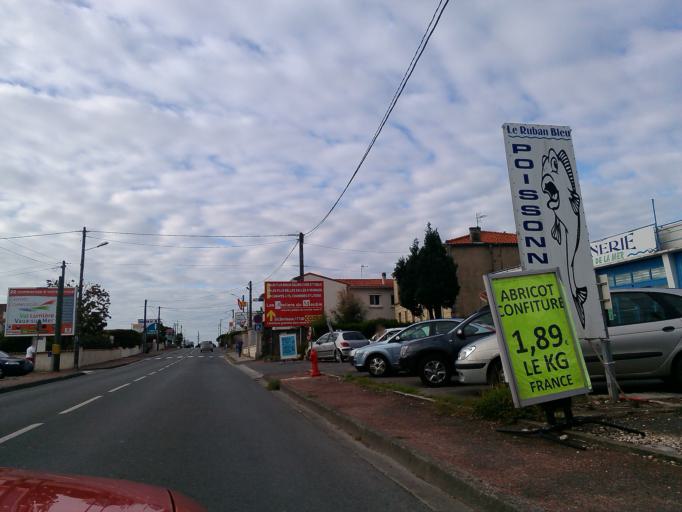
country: FR
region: Poitou-Charentes
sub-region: Departement de la Charente-Maritime
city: Royan
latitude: 45.6437
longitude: -1.0249
